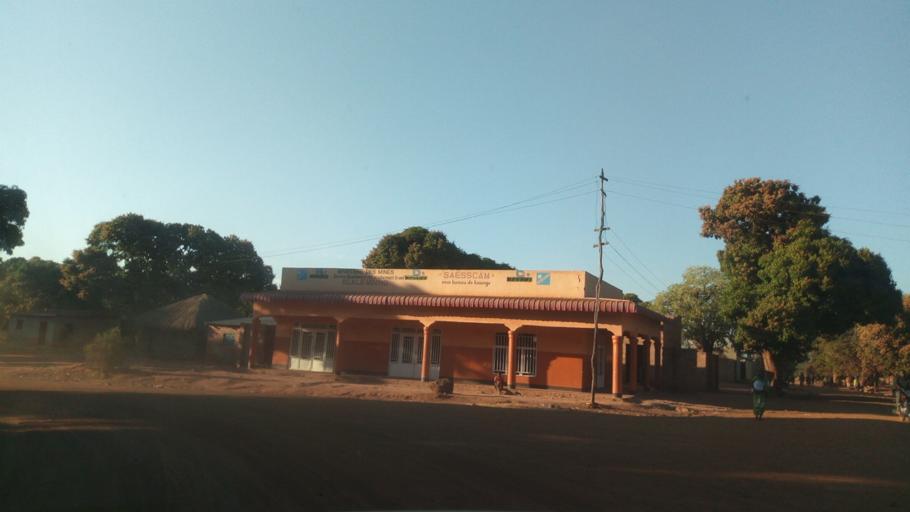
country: ZM
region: Luapula
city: Mwense
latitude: -10.3824
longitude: 28.6143
